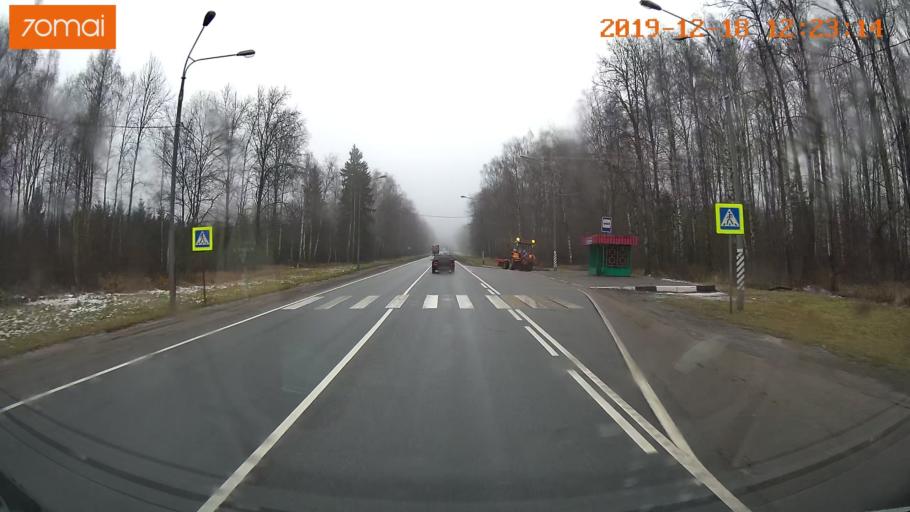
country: RU
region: Moskovskaya
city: Novopetrovskoye
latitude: 56.0116
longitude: 36.4906
